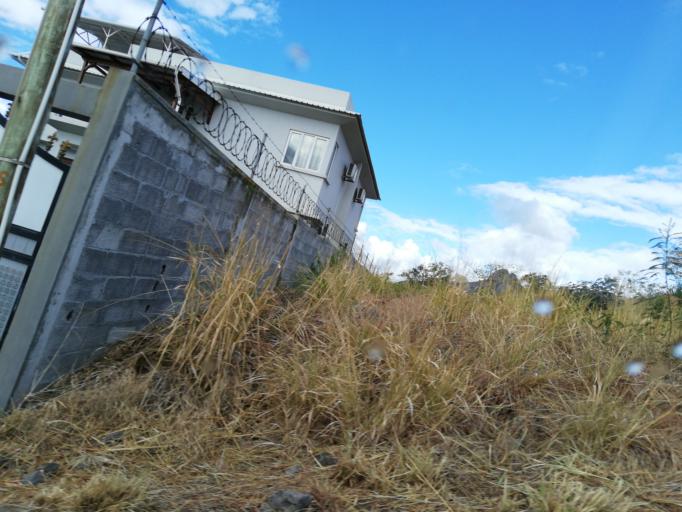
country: MU
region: Black River
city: Petite Riviere
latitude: -20.2034
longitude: 57.4604
